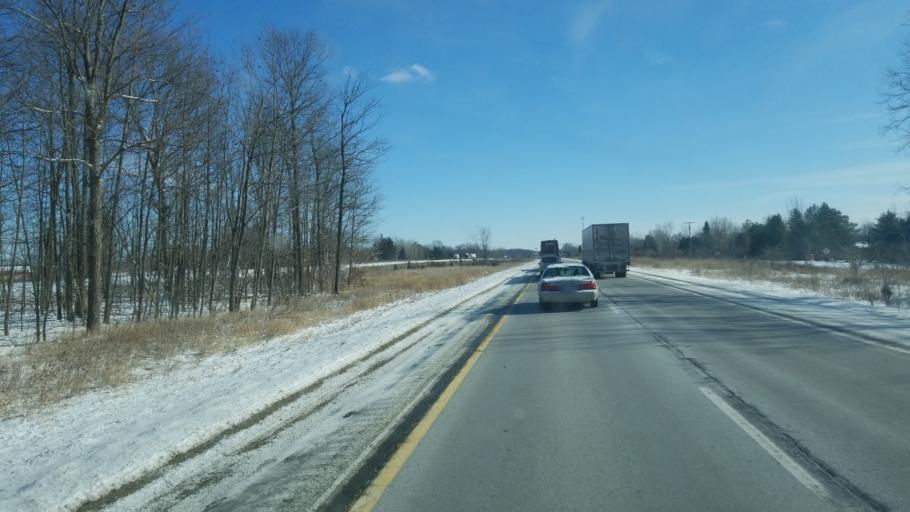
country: US
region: Michigan
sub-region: Livingston County
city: Fowlerville
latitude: 42.6364
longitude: -84.0269
